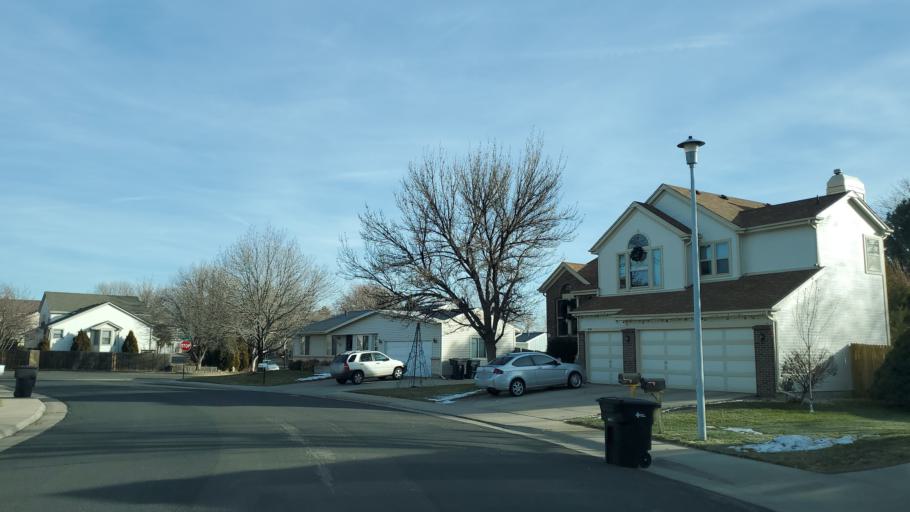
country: US
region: Colorado
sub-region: Adams County
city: Northglenn
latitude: 39.9050
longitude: -104.9537
